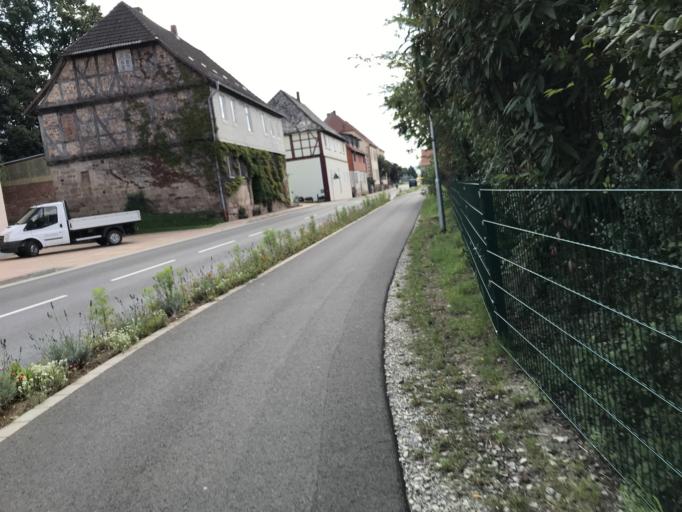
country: DE
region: Thuringia
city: Wahlhausen
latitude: 51.2926
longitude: 9.9779
